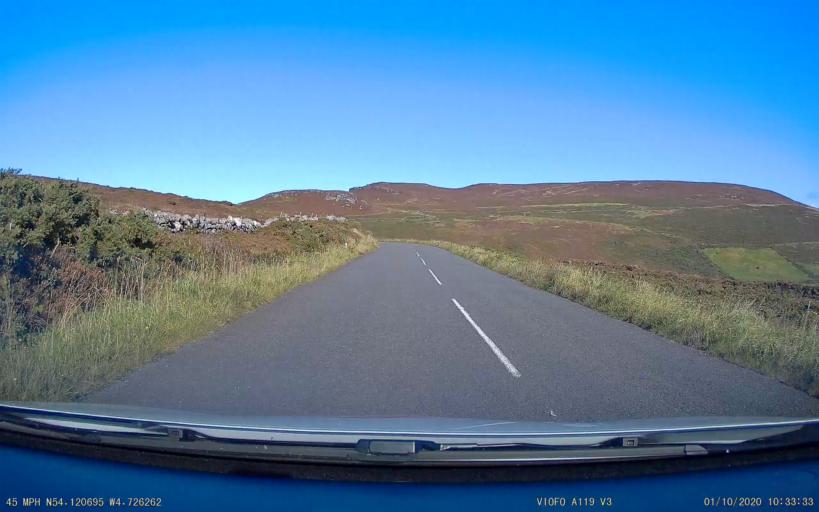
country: IM
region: Port Erin
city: Port Erin
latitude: 54.1207
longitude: -4.7260
